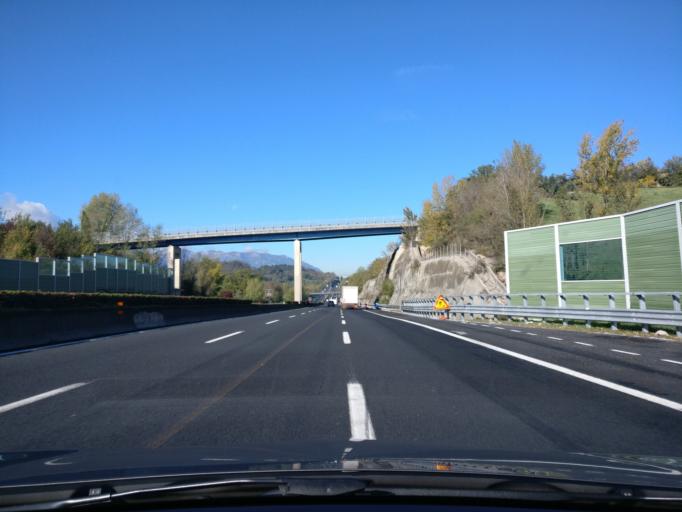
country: IT
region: Latium
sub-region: Provincia di Frosinone
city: Arnara
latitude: 41.5733
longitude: 13.3764
